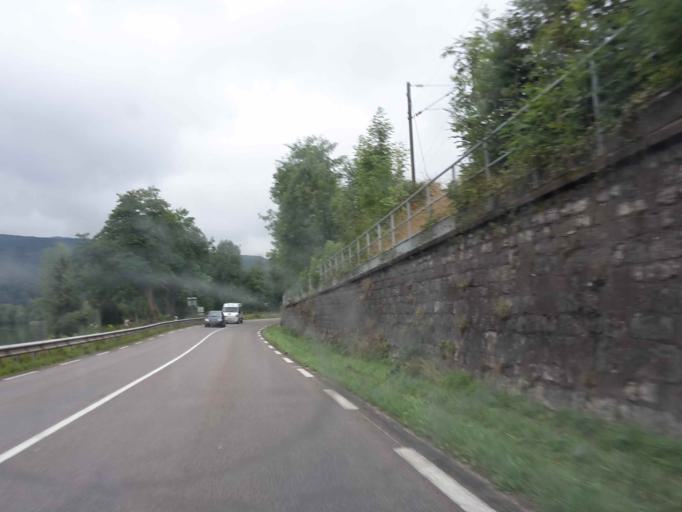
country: FR
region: Franche-Comte
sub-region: Departement du Doubs
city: Novillars
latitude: 47.2790
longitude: 6.1227
